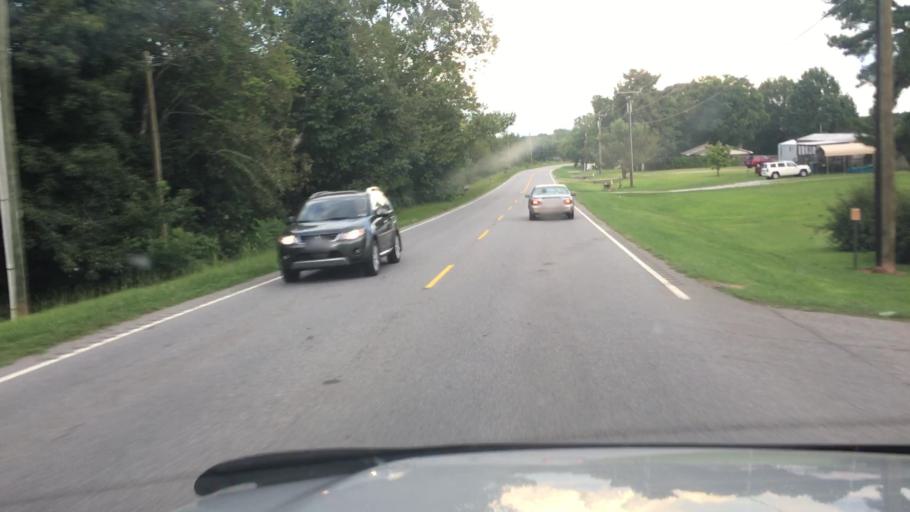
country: US
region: South Carolina
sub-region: Cherokee County
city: Gaffney
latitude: 35.1267
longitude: -81.7325
